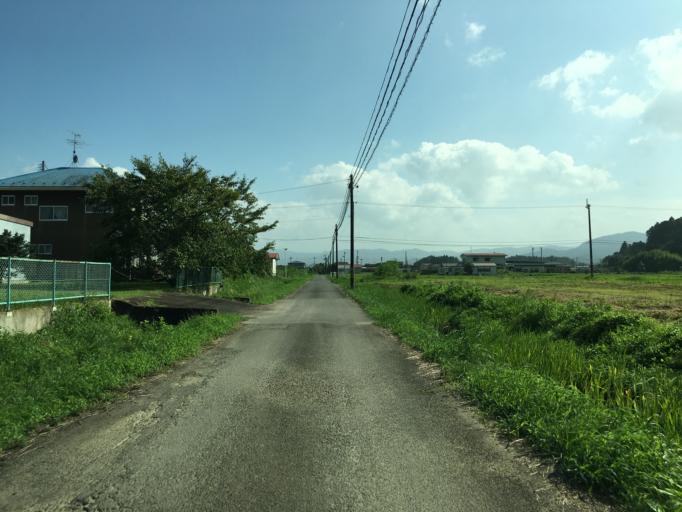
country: JP
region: Miyagi
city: Kakuda
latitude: 37.9521
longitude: 140.7800
